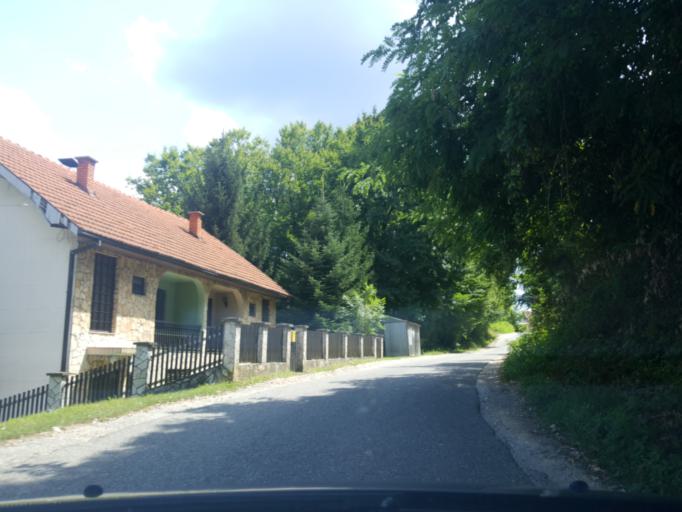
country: RS
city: Trsic
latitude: 44.5227
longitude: 19.2245
